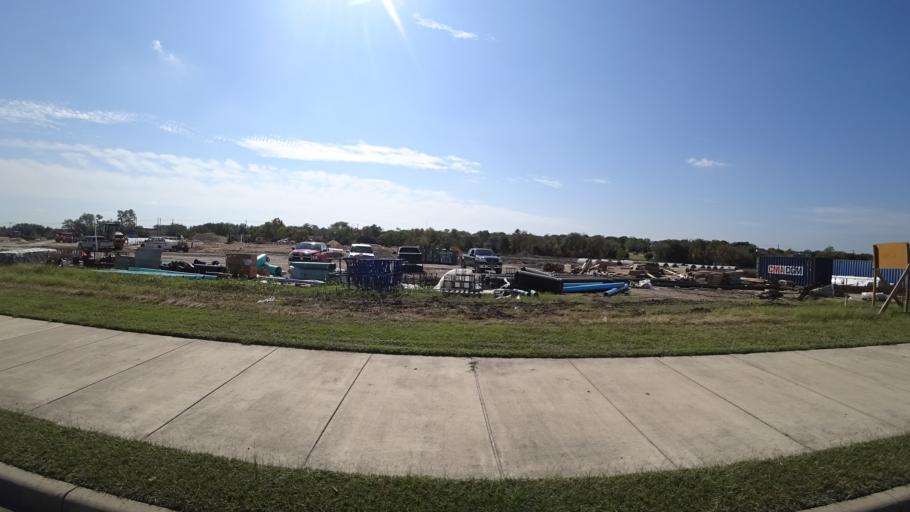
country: US
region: Texas
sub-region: Travis County
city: Pflugerville
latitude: 30.4224
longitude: -97.6216
